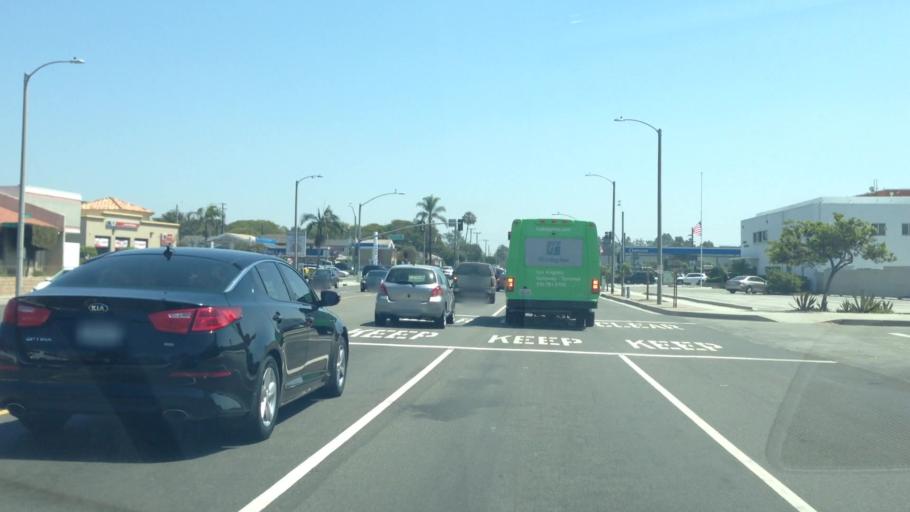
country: US
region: California
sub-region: Los Angeles County
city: Torrance
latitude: 33.8312
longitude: -118.3301
